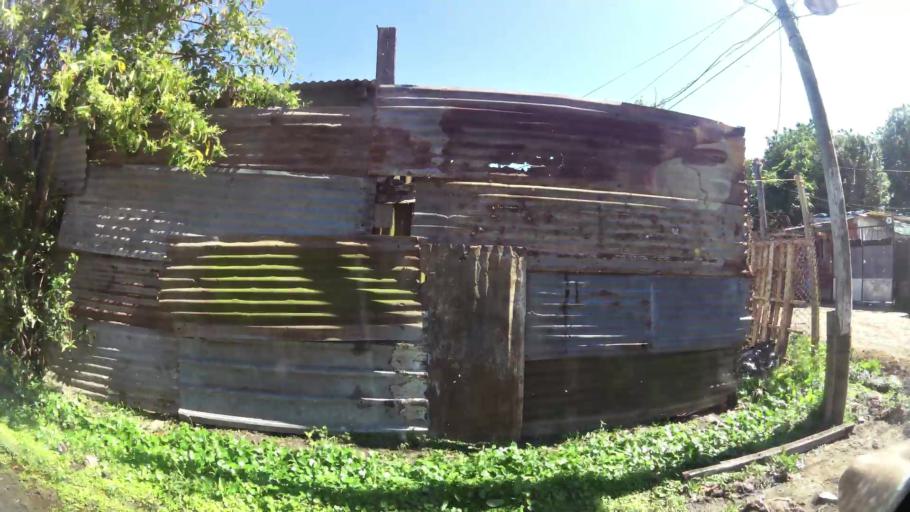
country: AR
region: Santa Fe
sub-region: Departamento de Rosario
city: Rosario
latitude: -32.9751
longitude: -60.6900
